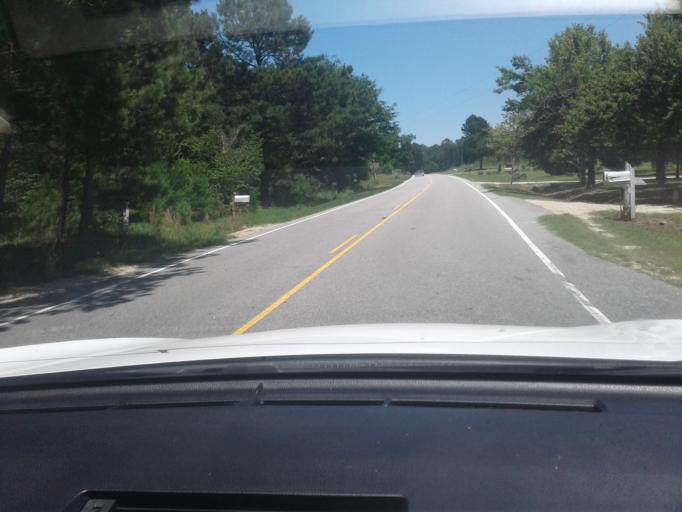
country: US
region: North Carolina
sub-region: Harnett County
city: Lillington
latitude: 35.3682
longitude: -78.8852
